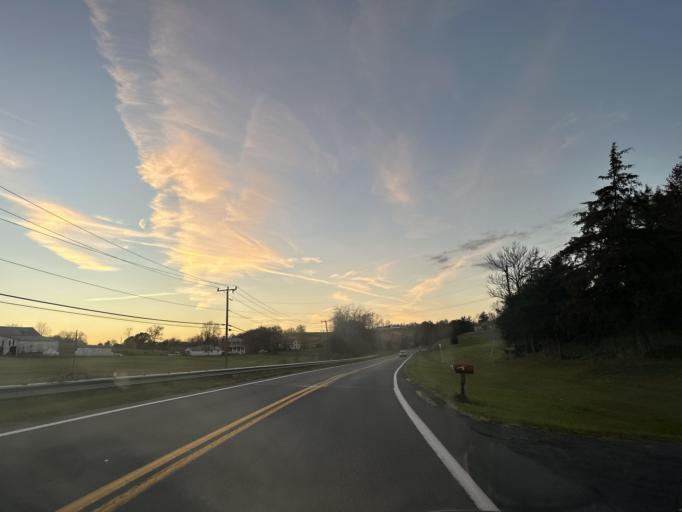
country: US
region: Virginia
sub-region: Rockingham County
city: Bridgewater
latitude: 38.4207
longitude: -79.0104
